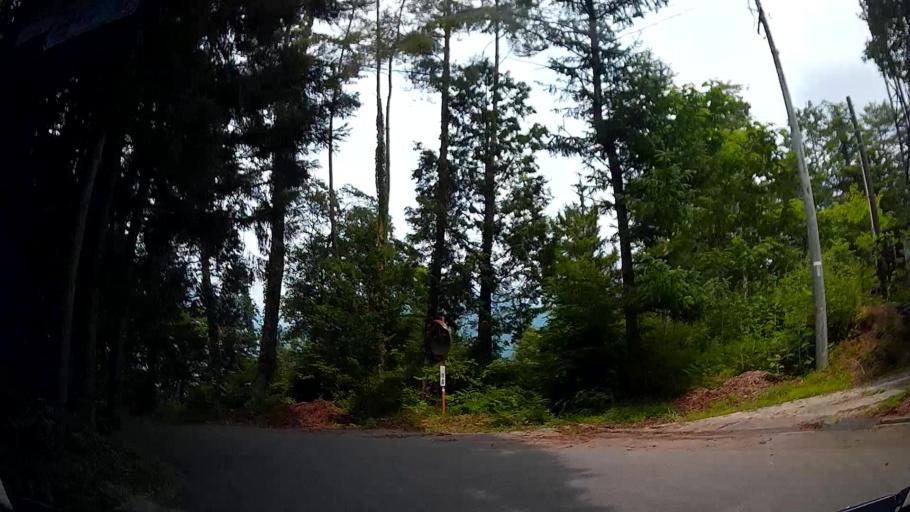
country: JP
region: Nagano
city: Iida
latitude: 35.2902
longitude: 137.9258
